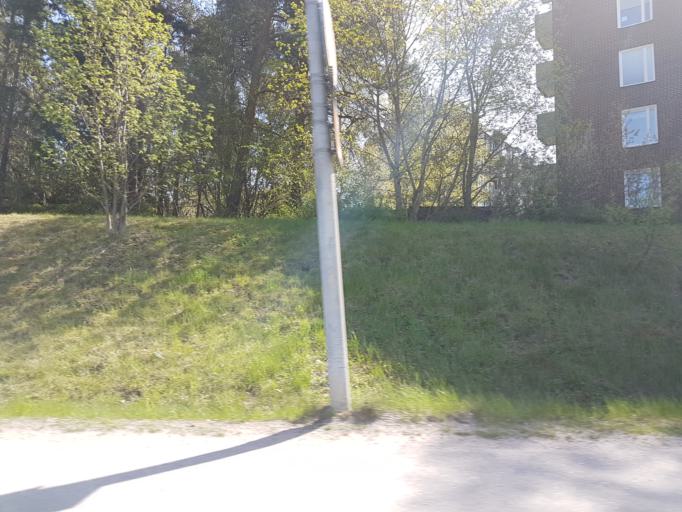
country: SE
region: Stockholm
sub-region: Stockholms Kommun
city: Bromma
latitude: 59.3297
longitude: 17.9172
